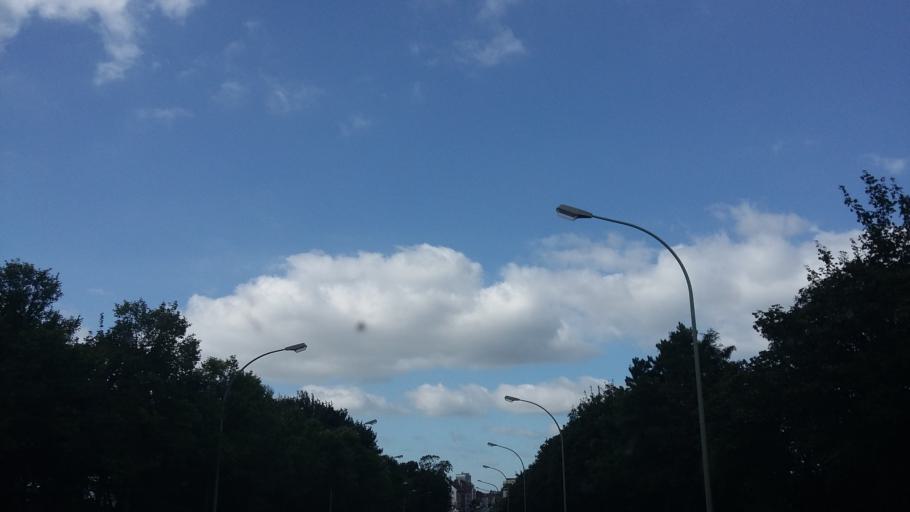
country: DE
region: Bremen
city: Bremerhaven
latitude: 53.5235
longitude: 8.5904
